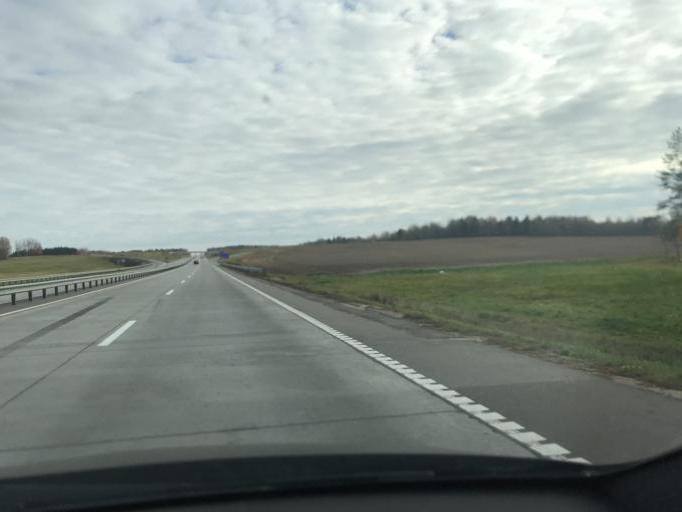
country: BY
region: Minsk
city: Zaslawye
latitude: 54.0638
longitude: 27.3411
